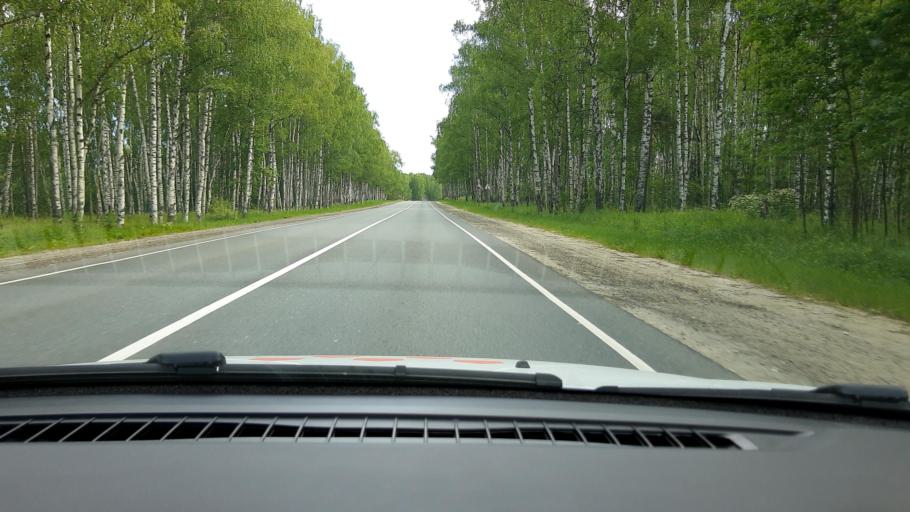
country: RU
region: Nizjnij Novgorod
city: Linda
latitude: 56.6722
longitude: 44.1425
